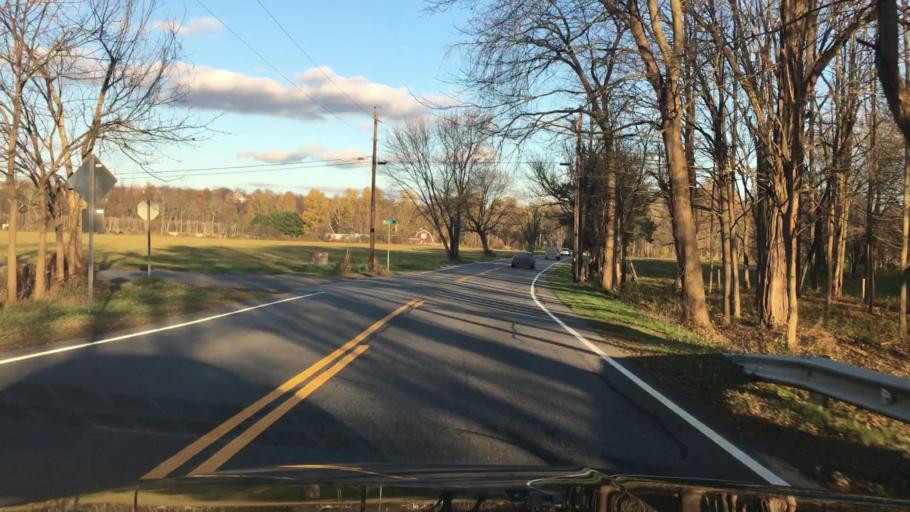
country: US
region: New York
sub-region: Dutchess County
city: Hillside Lake
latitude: 41.6451
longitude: -73.7852
